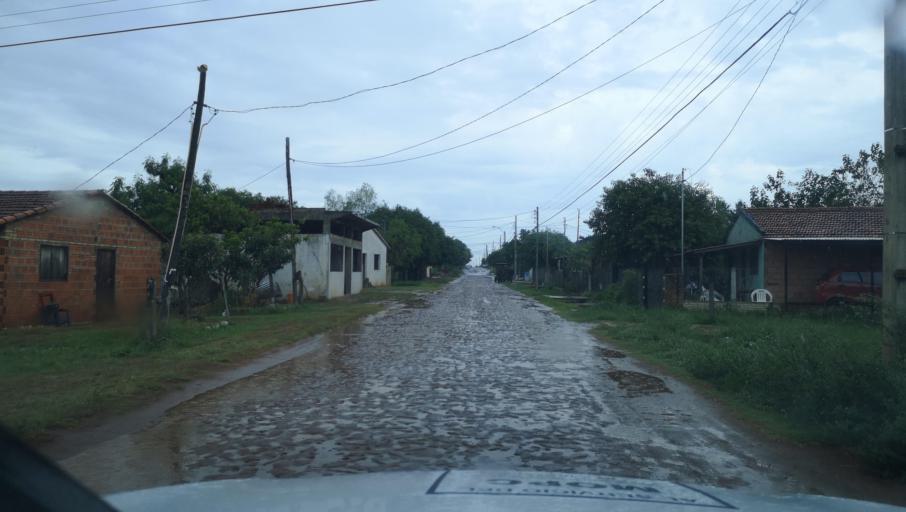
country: PY
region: Misiones
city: Santa Maria
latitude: -26.8973
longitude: -57.0356
